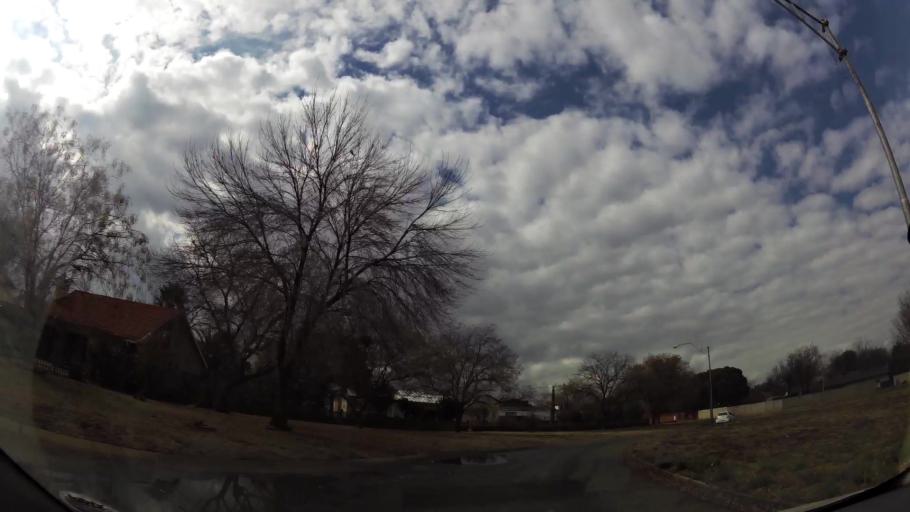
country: ZA
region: Gauteng
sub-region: Sedibeng District Municipality
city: Vereeniging
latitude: -26.6537
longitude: 27.9906
